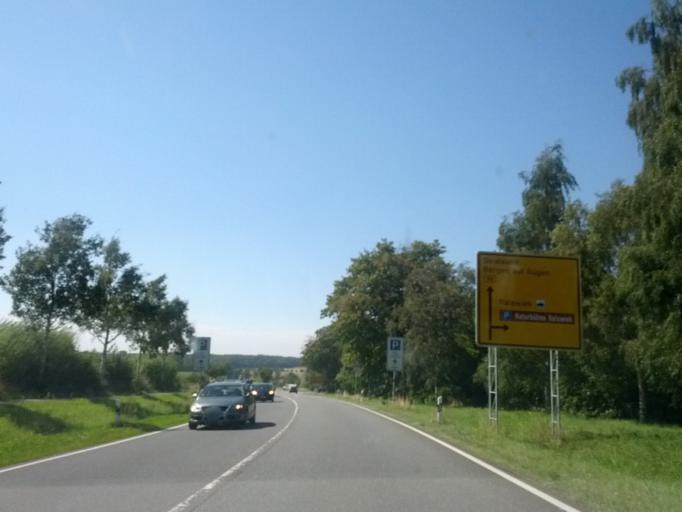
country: DE
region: Mecklenburg-Vorpommern
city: Bergen auf Ruegen
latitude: 54.4652
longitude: 13.4560
